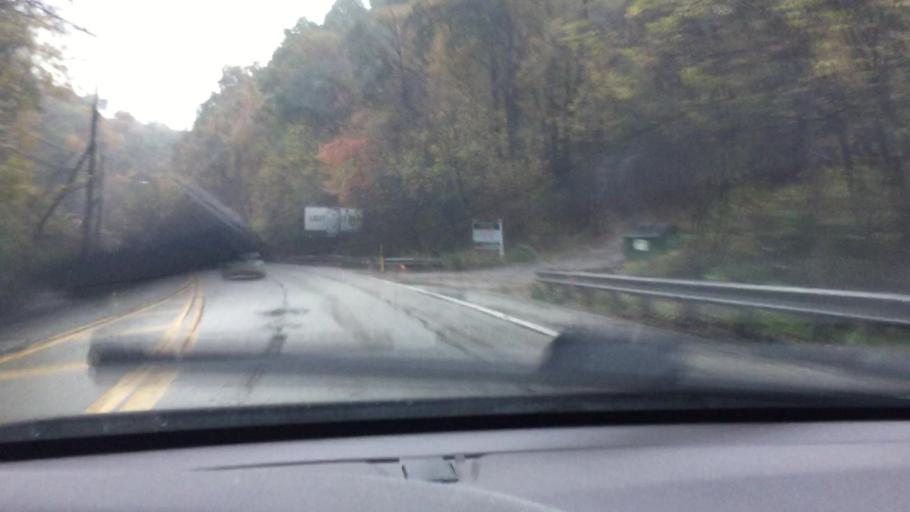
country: US
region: Pennsylvania
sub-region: Allegheny County
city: West Homestead
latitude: 40.3740
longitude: -79.9264
